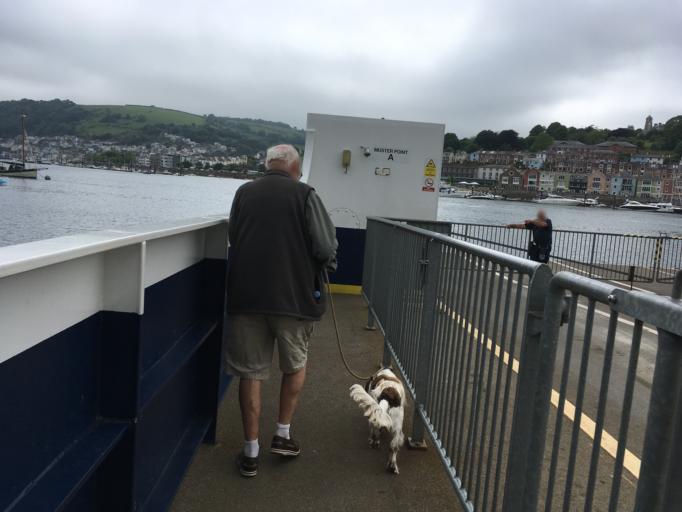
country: GB
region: England
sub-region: Devon
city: Dartmouth
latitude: 50.3594
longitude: -3.5737
